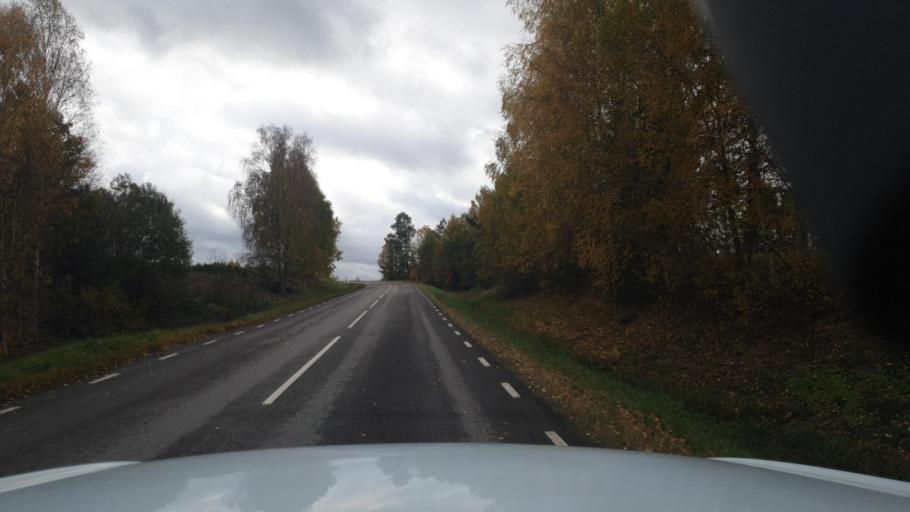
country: SE
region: Vaermland
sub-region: Sunne Kommun
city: Sunne
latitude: 59.7906
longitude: 13.0813
